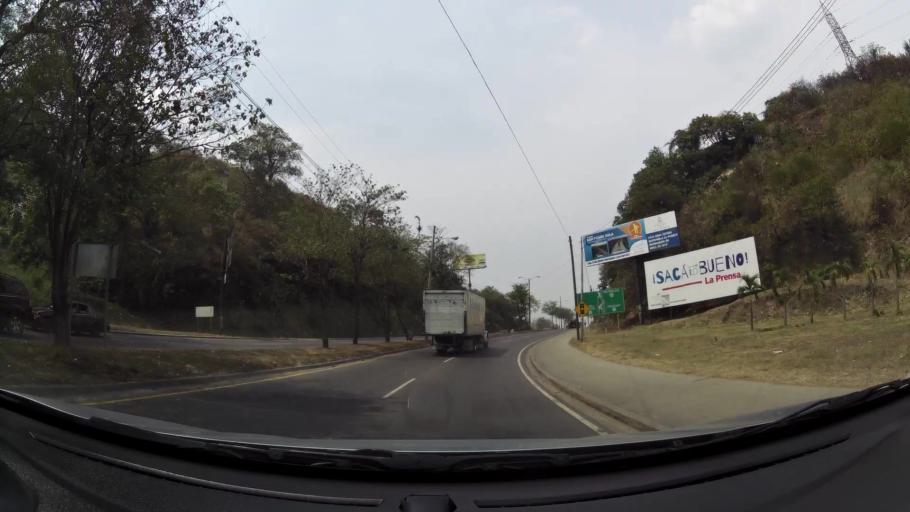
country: HN
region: Cortes
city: El Maranon
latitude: 15.4295
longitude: -88.0229
